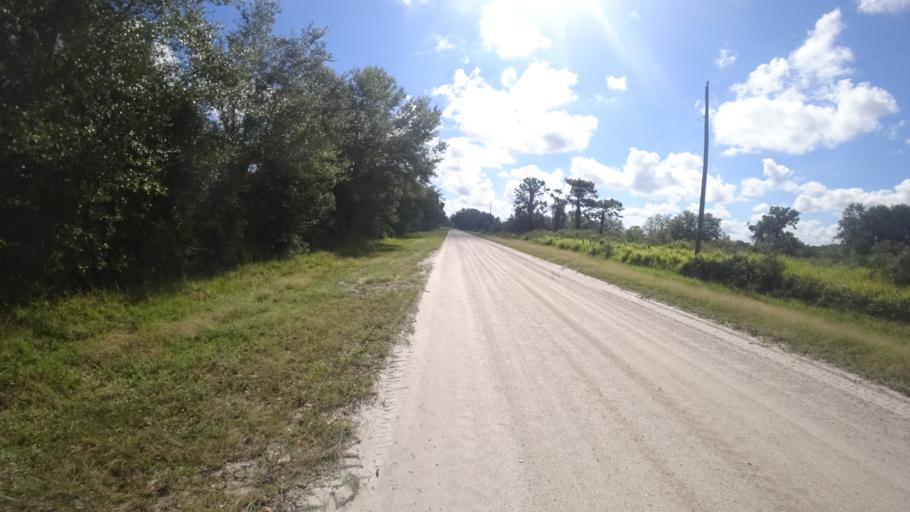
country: US
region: Florida
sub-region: DeSoto County
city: Arcadia
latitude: 27.3573
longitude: -82.1291
